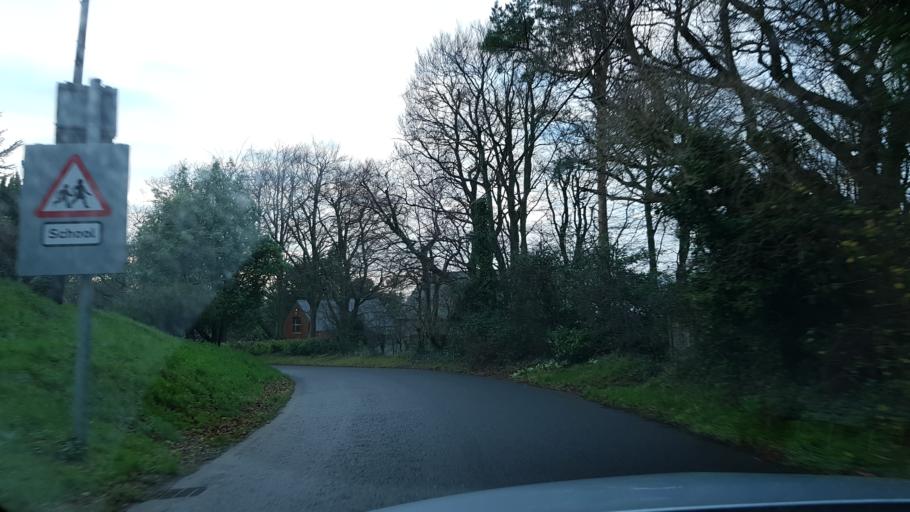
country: GB
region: Northern Ireland
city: Holywood
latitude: 54.6401
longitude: -5.8125
